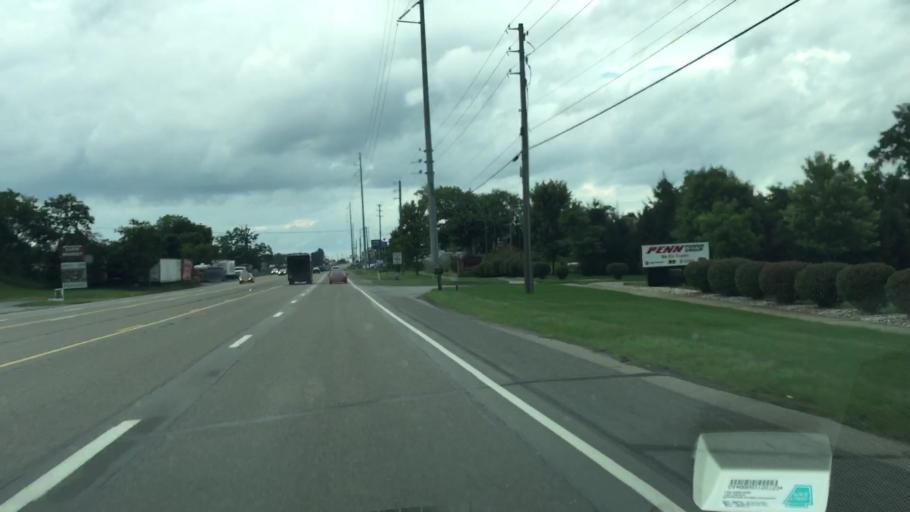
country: US
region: Pennsylvania
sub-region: Butler County
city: Fox Run
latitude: 40.7433
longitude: -80.1129
